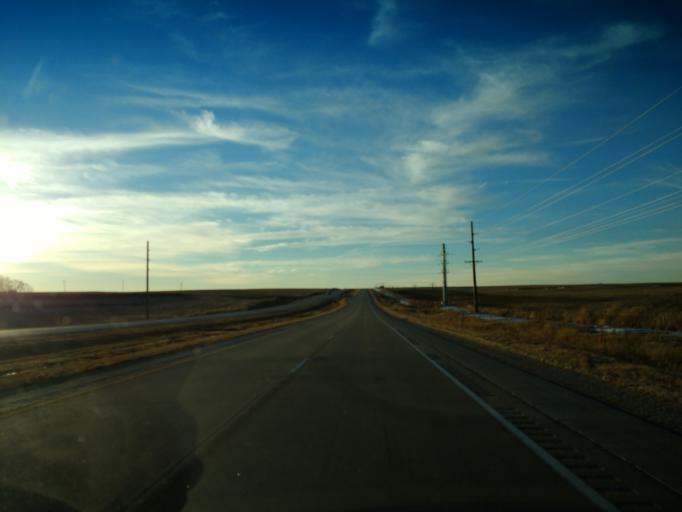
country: US
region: Iowa
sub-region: Ida County
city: Holstein
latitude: 42.4751
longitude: -95.4929
